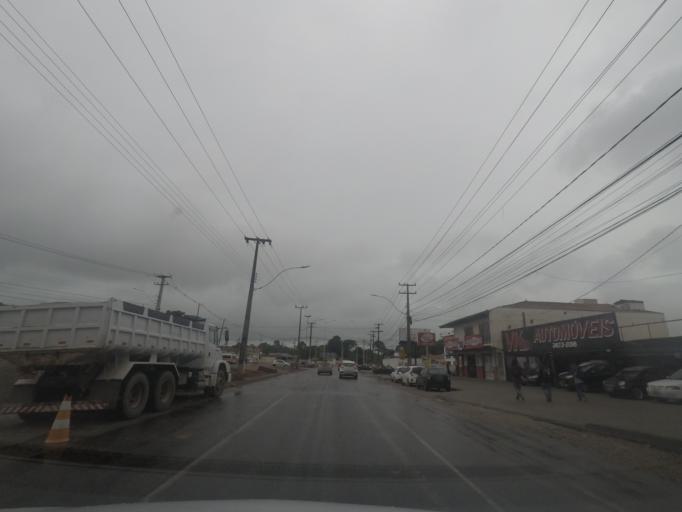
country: BR
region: Parana
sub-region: Piraquara
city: Piraquara
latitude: -25.4525
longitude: -49.0713
